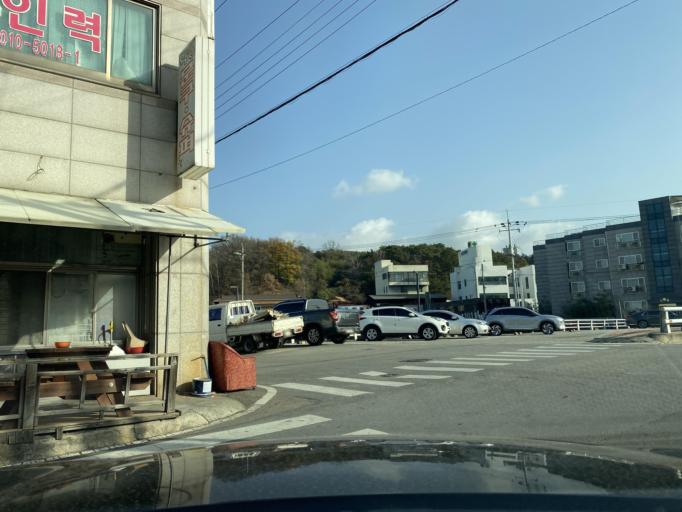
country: KR
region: Chungcheongnam-do
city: Yesan
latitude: 36.6795
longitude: 126.8336
